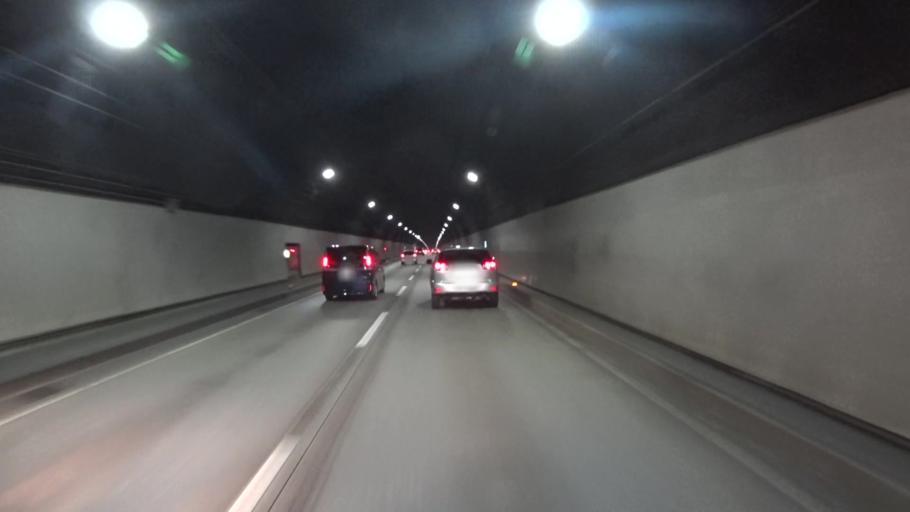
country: JP
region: Shiga Prefecture
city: Otsu-shi
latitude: 35.0153
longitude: 135.8452
